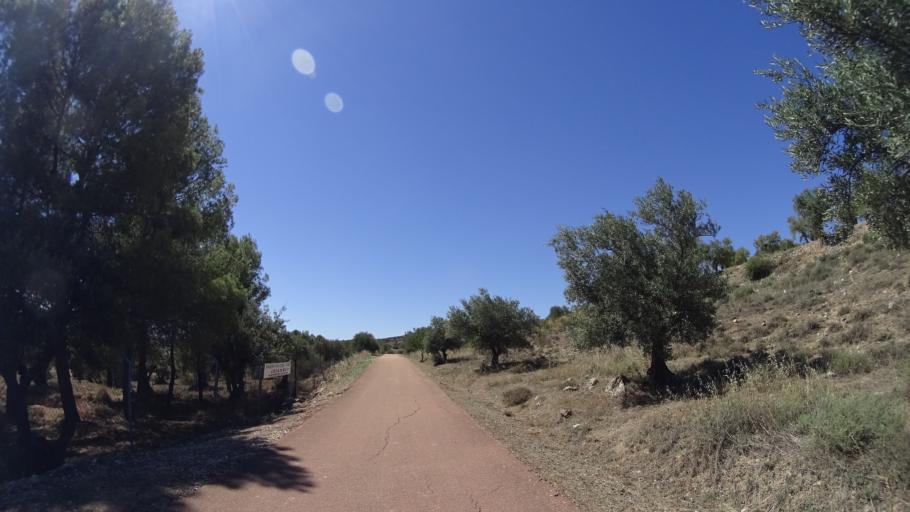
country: ES
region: Madrid
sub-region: Provincia de Madrid
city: Perales de Tajuna
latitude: 40.2315
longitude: -3.3813
